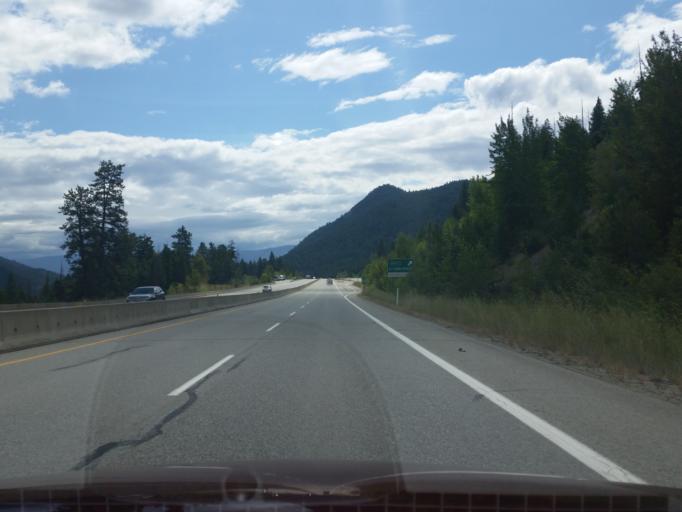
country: CA
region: British Columbia
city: Peachland
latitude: 49.8256
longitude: -119.7925
